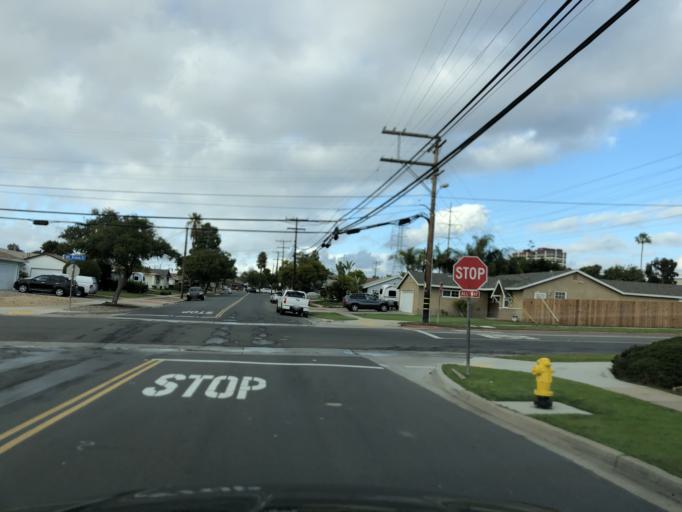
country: US
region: California
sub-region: San Diego County
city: La Jolla
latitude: 32.8159
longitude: -117.1852
